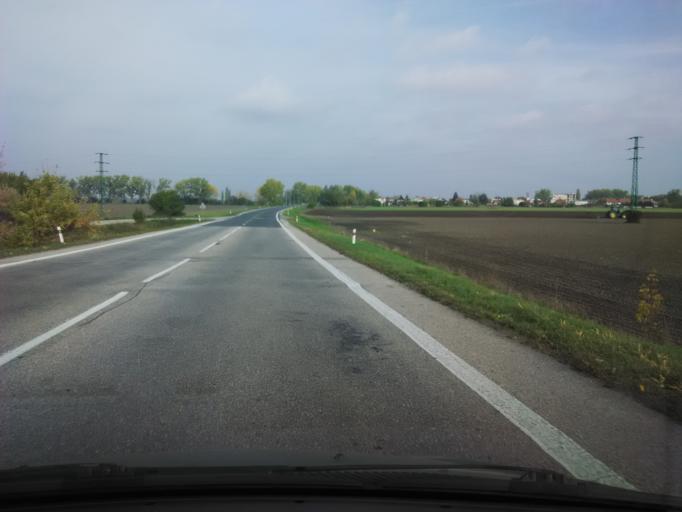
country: SK
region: Nitriansky
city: Komarno
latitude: 47.7802
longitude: 18.1622
